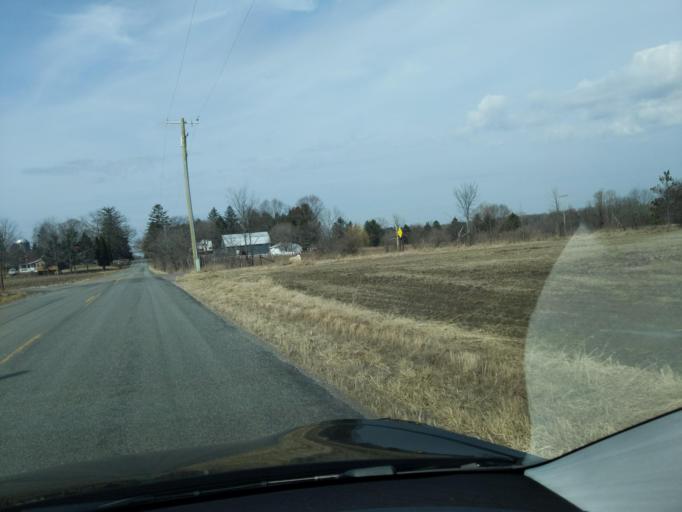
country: US
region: Michigan
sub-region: Ingham County
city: Williamston
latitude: 42.6585
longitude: -84.3402
